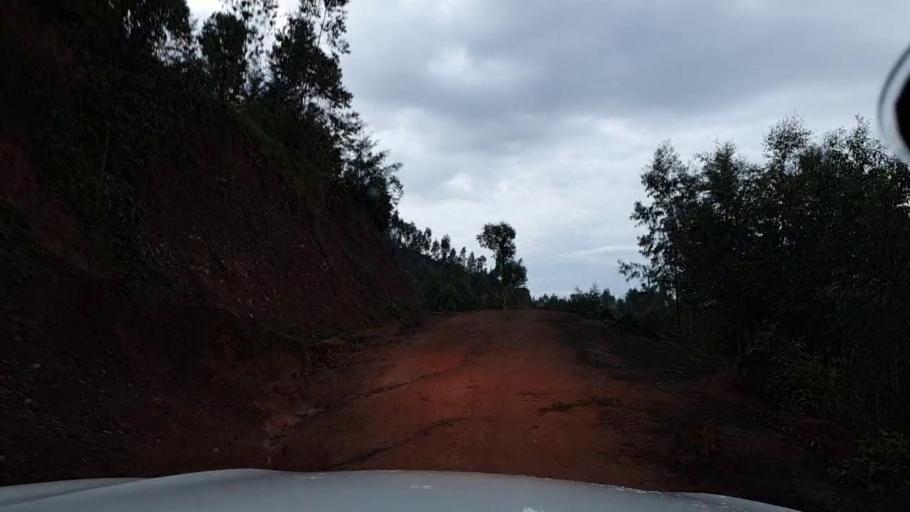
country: BI
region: Kayanza
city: Kayanza
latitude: -2.7194
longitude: 29.5446
